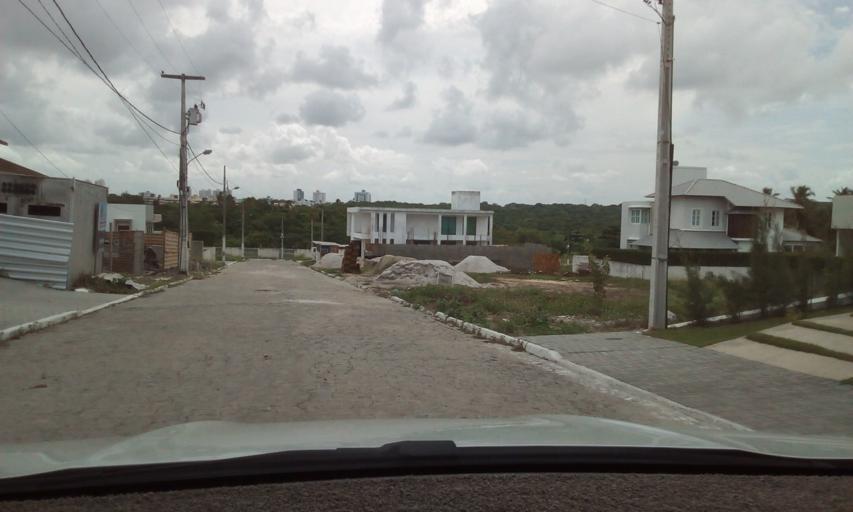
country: BR
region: Paraiba
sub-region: Joao Pessoa
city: Joao Pessoa
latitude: -7.1408
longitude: -34.8282
